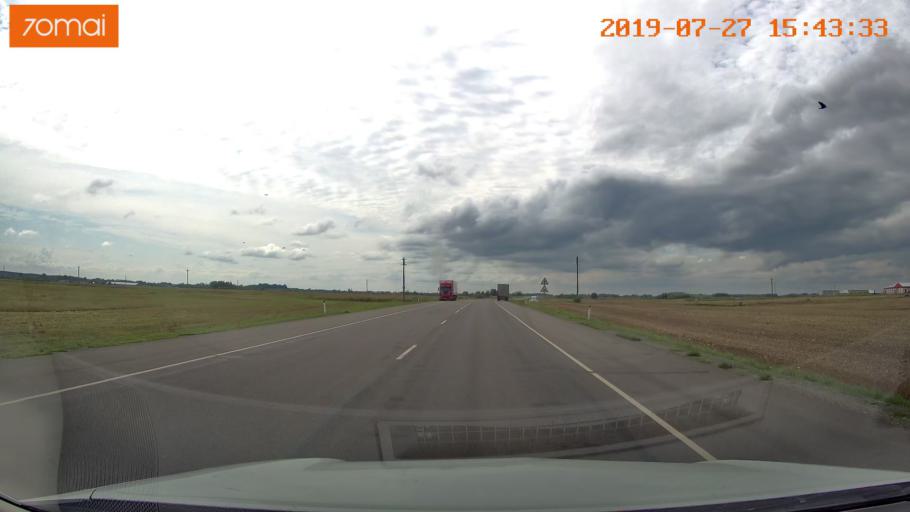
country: RU
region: Kaliningrad
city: Gusev
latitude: 54.6149
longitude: 22.1898
